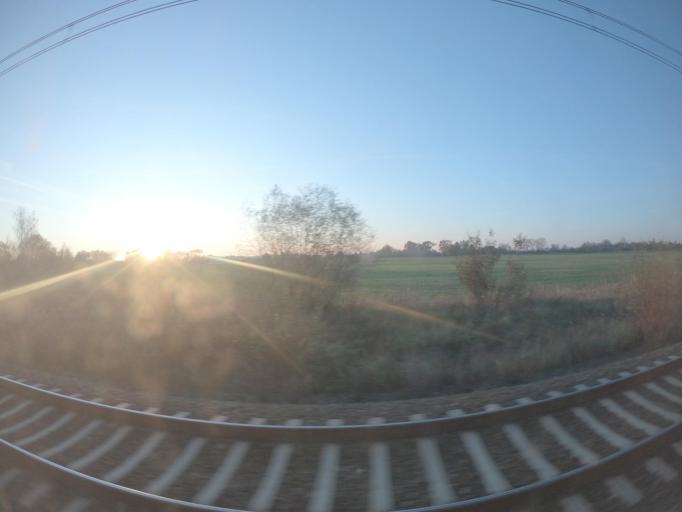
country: PL
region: Lubusz
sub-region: Powiat slubicki
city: Gorzyca
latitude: 52.5395
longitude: 14.6508
